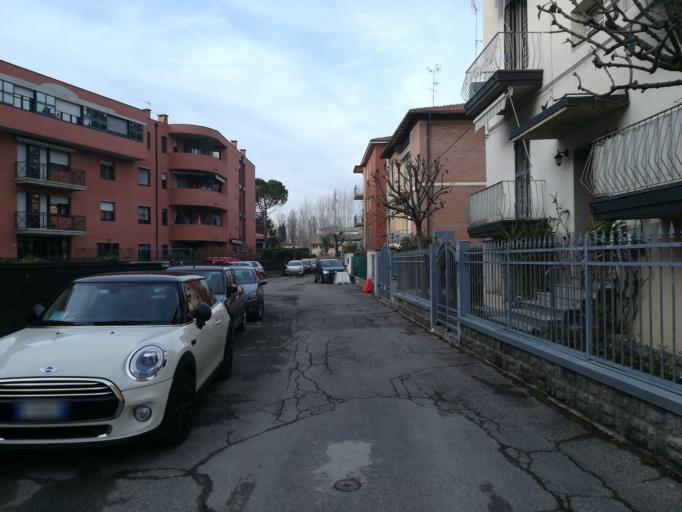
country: IT
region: Emilia-Romagna
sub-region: Provincia di Bologna
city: Progresso
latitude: 44.5439
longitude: 11.3534
